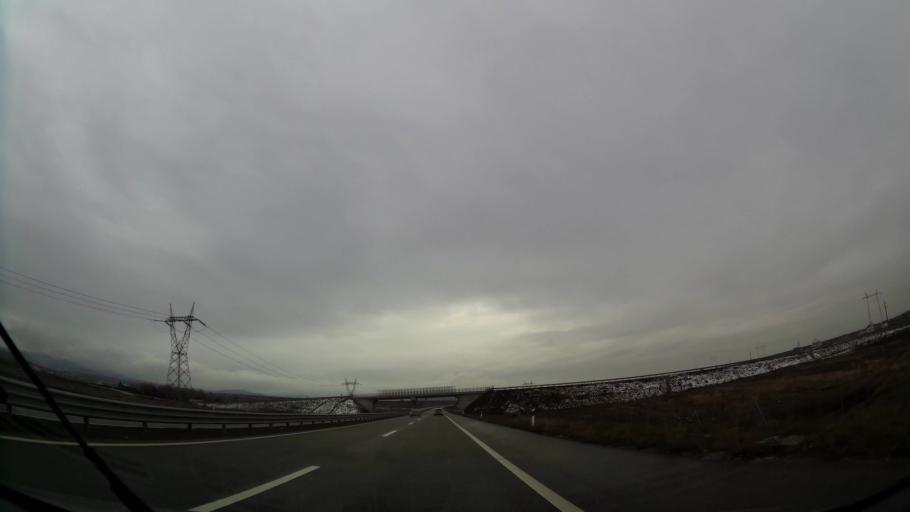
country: XK
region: Pristina
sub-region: Lipjan
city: Lipljan
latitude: 42.5121
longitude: 21.1775
